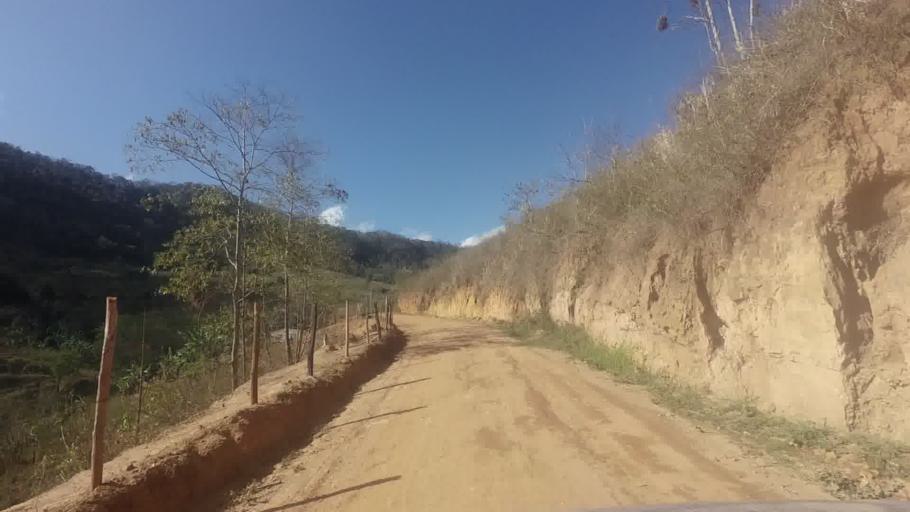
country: BR
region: Espirito Santo
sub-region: Sao Jose Do Calcado
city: Sao Jose do Calcado
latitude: -21.0335
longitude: -41.5961
